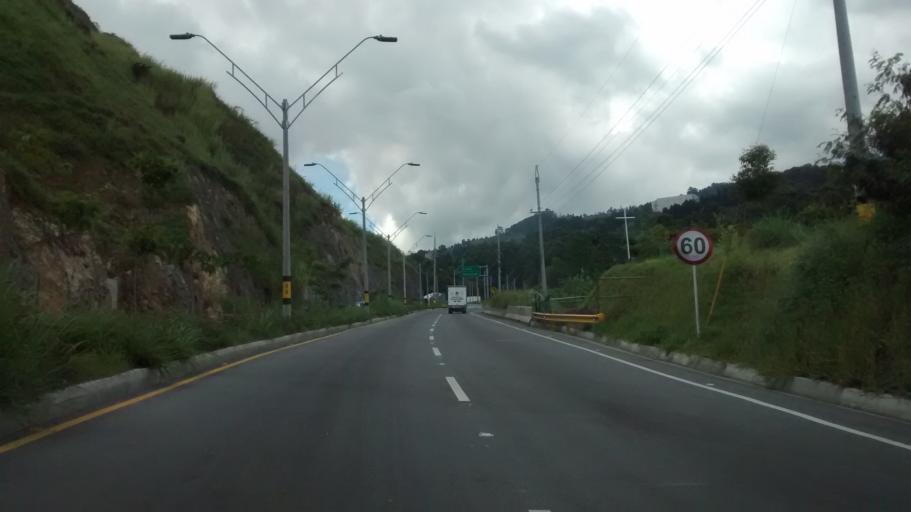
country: CO
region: Antioquia
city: Medellin
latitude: 6.2728
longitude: -75.6199
